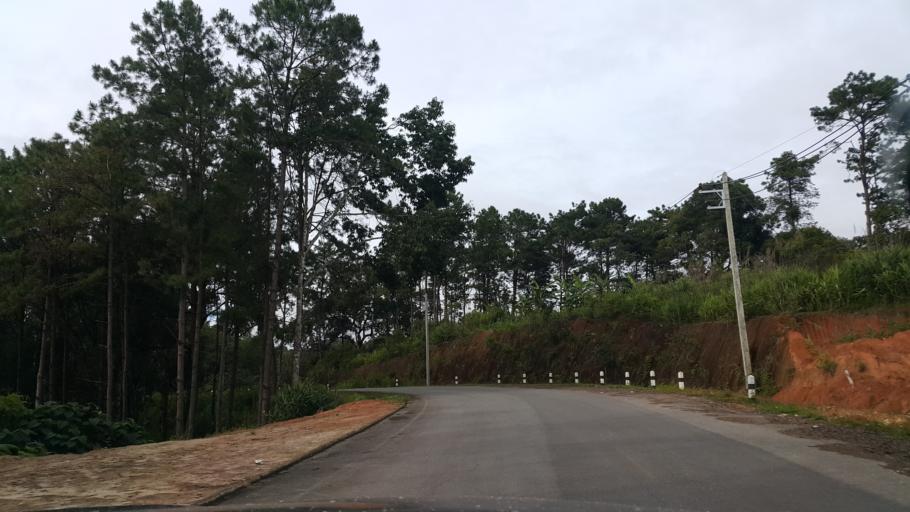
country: TH
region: Chiang Mai
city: Chaem Luang
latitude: 18.9360
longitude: 98.4642
